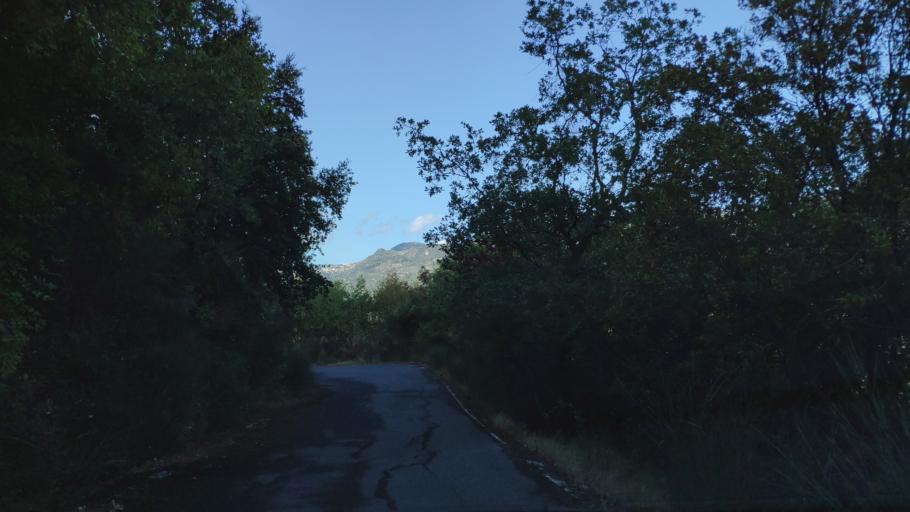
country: GR
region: Peloponnese
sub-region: Nomos Arkadias
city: Dimitsana
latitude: 37.5528
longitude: 22.0452
